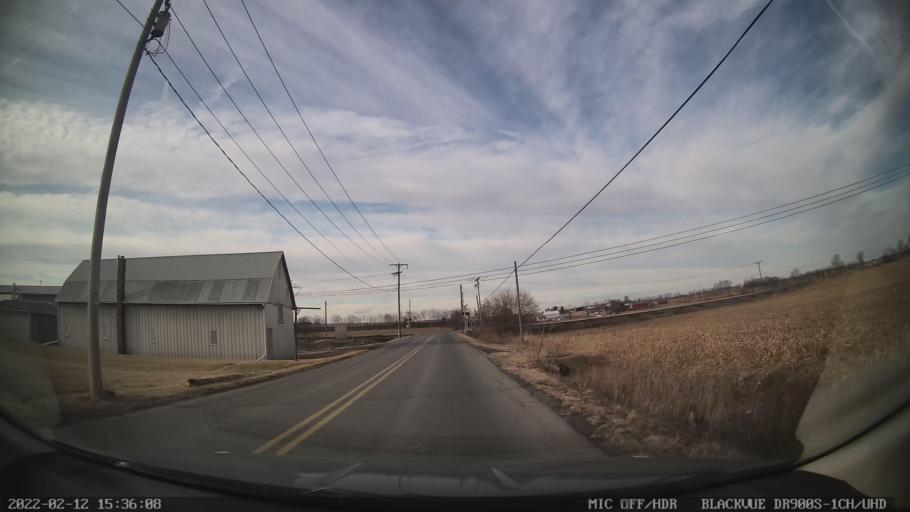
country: US
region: Pennsylvania
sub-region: Berks County
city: Topton
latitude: 40.4890
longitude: -75.7367
